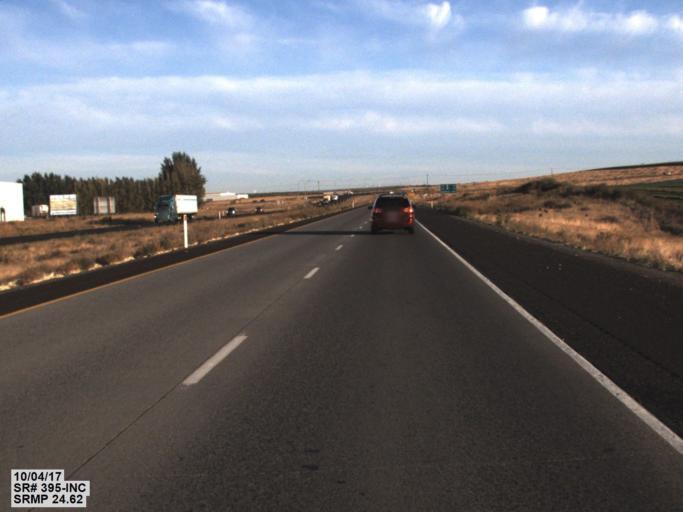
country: US
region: Washington
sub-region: Franklin County
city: Pasco
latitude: 46.2782
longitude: -119.0911
